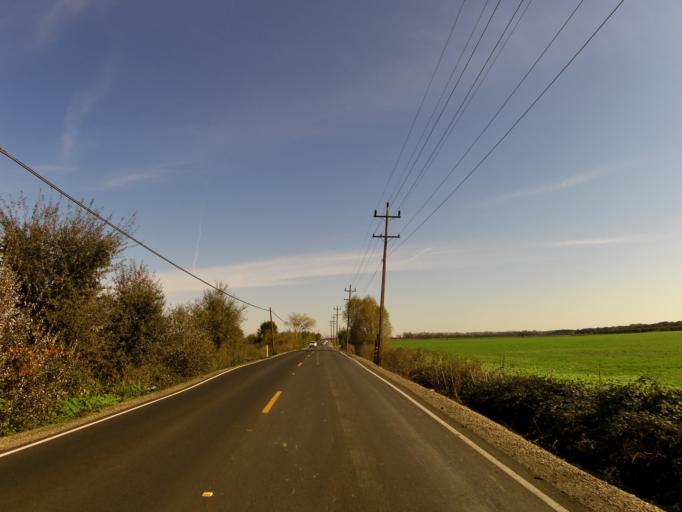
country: US
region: California
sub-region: Sacramento County
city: Walnut Grove
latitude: 38.2769
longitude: -121.4817
